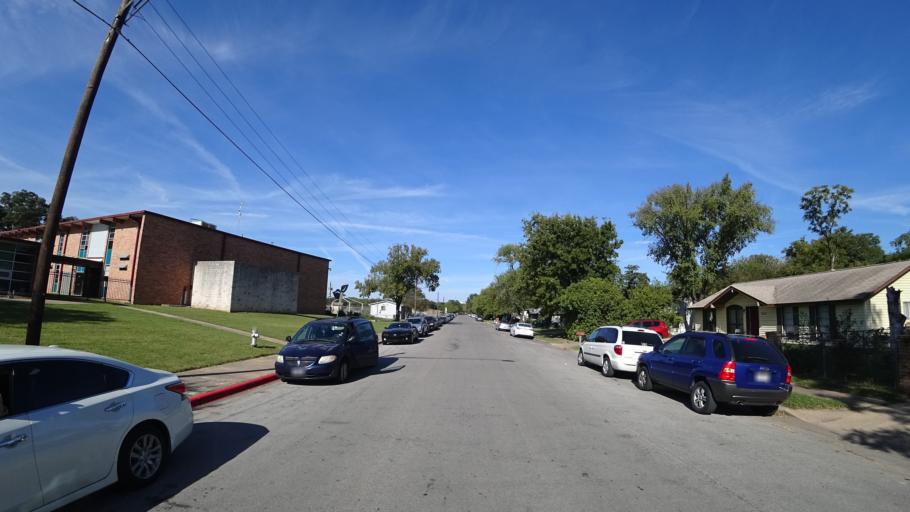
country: US
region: Texas
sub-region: Travis County
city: Austin
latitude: 30.2578
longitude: -97.6804
